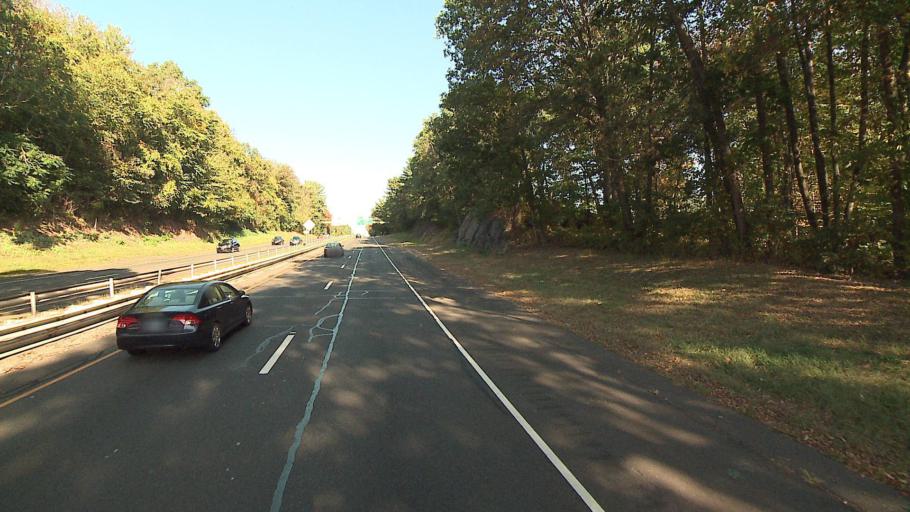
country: US
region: Connecticut
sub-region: New Haven County
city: City of Milford (balance)
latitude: 41.2379
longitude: -73.0755
